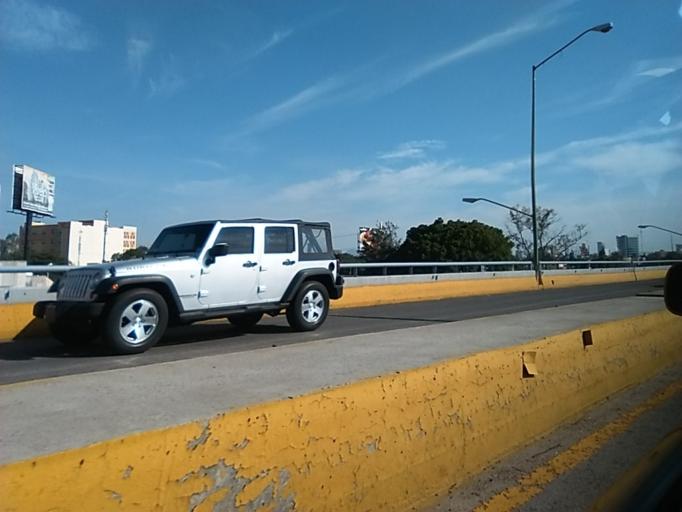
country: MX
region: Jalisco
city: Guadalajara
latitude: 20.6587
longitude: -103.3851
